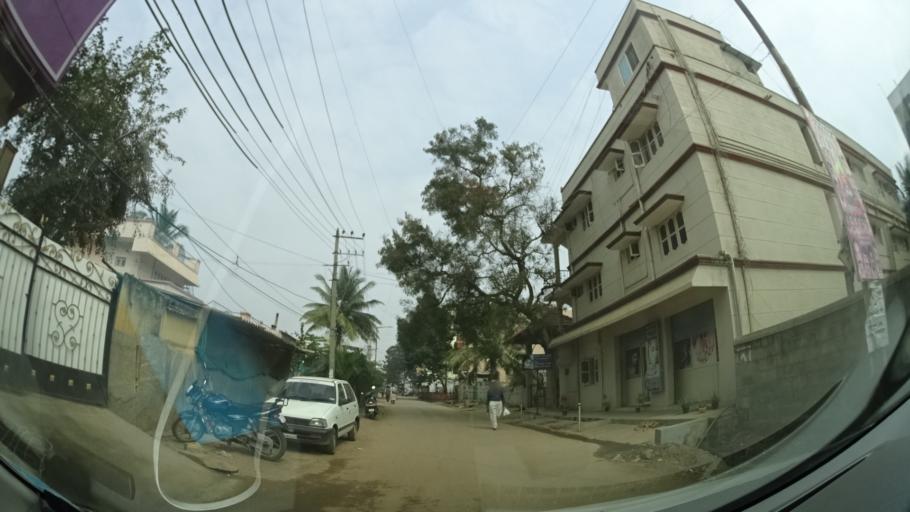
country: IN
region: Karnataka
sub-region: Bangalore Rural
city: Hoskote
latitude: 12.9660
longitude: 77.7537
